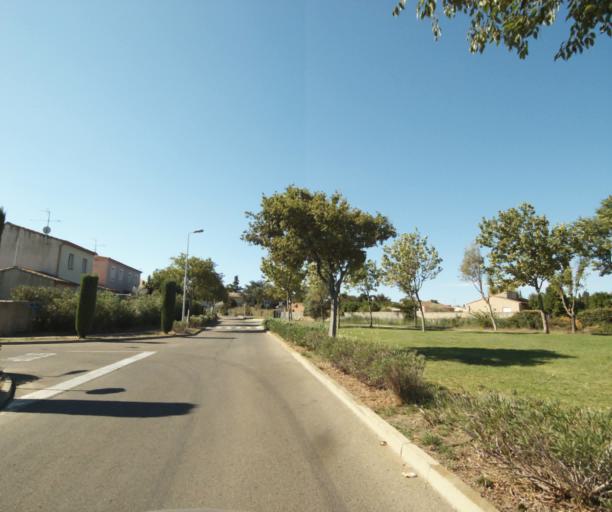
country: FR
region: Languedoc-Roussillon
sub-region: Departement du Gard
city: Bouillargues
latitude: 43.8048
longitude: 4.4263
